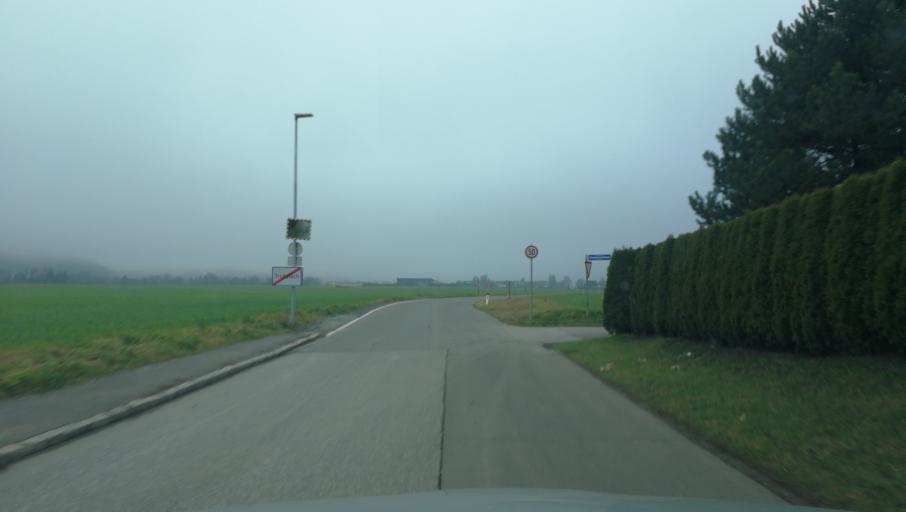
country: AT
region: Styria
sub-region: Politischer Bezirk Leoben
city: Trofaiach
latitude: 47.4320
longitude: 14.9858
